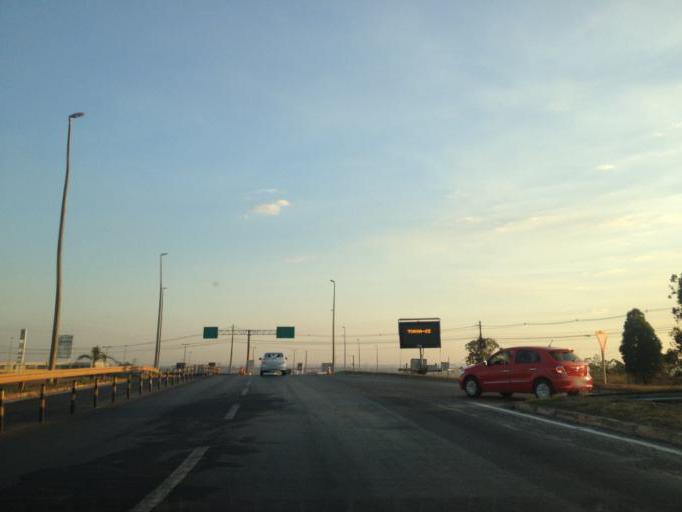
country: BR
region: Federal District
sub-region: Brasilia
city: Brasilia
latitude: -15.6877
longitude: -47.8605
